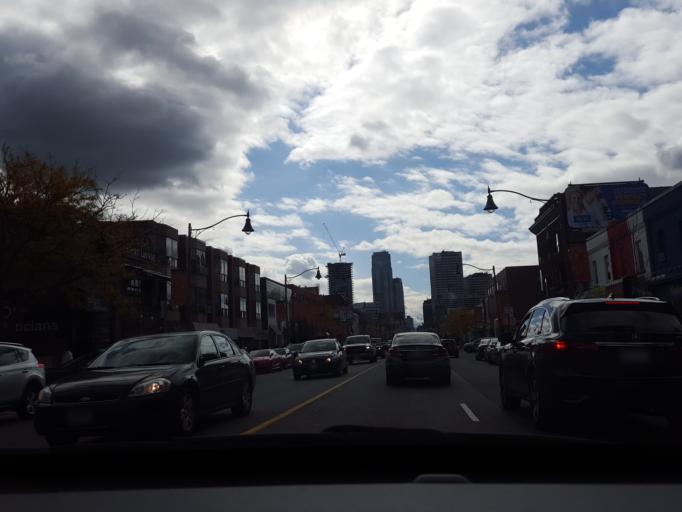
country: CA
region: Ontario
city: Toronto
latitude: 43.7161
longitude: -79.4004
